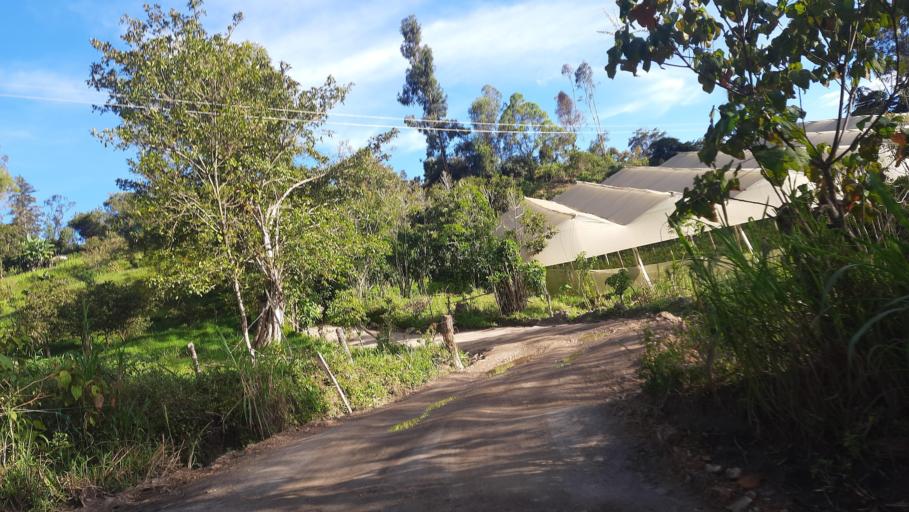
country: CO
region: Cundinamarca
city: Tenza
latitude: 5.1047
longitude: -73.4394
